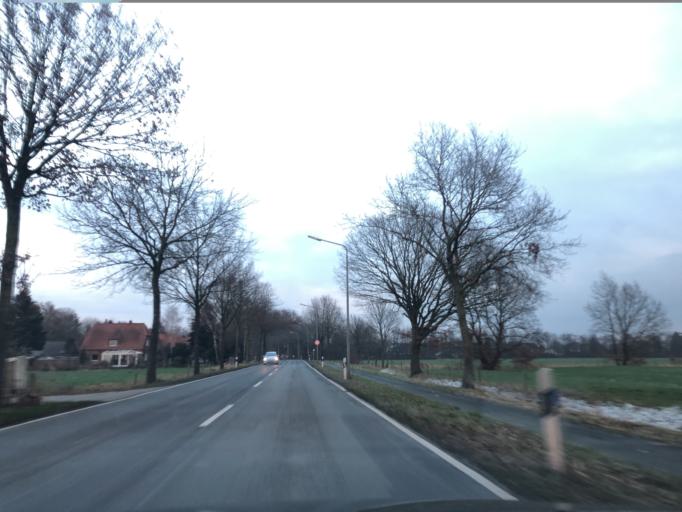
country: DE
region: Lower Saxony
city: Lemwerder
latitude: 53.1449
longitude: 8.5985
